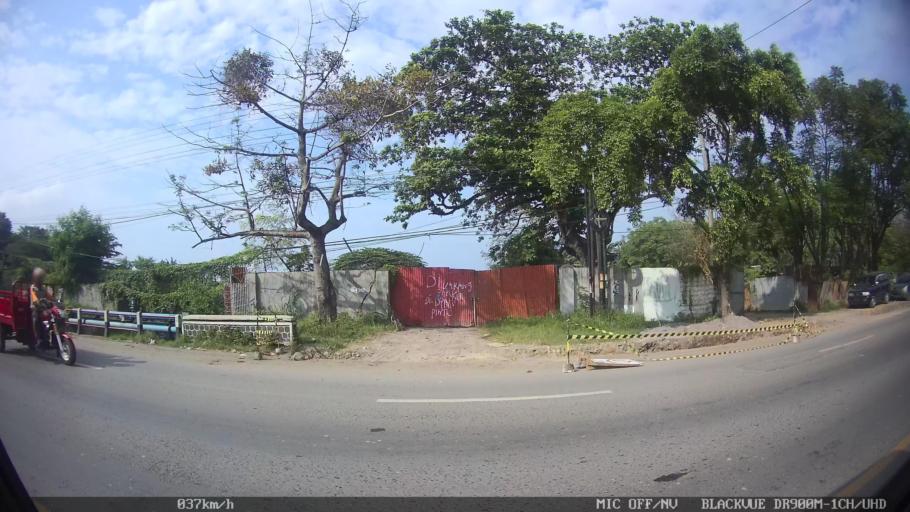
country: ID
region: Lampung
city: Panjang
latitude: -5.4537
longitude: 105.3090
